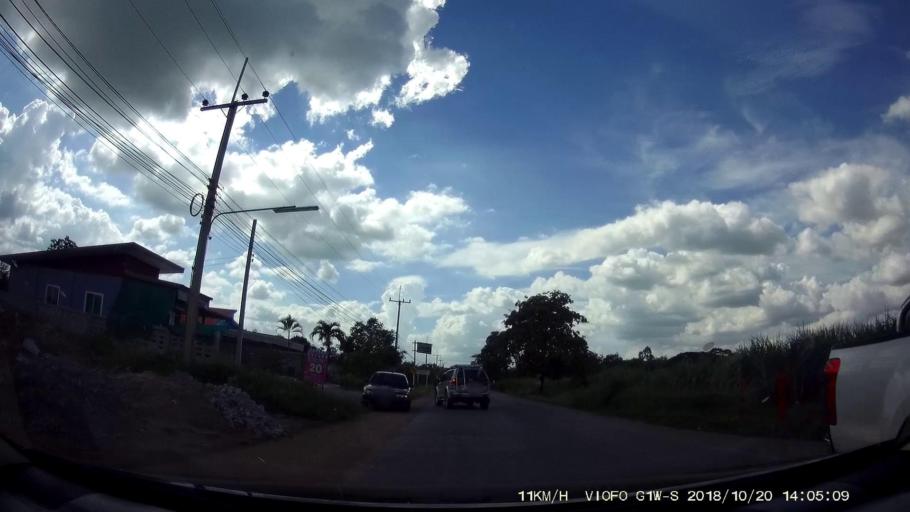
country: TH
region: Khon Kaen
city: Chum Phae
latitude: 16.4903
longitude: 102.1121
